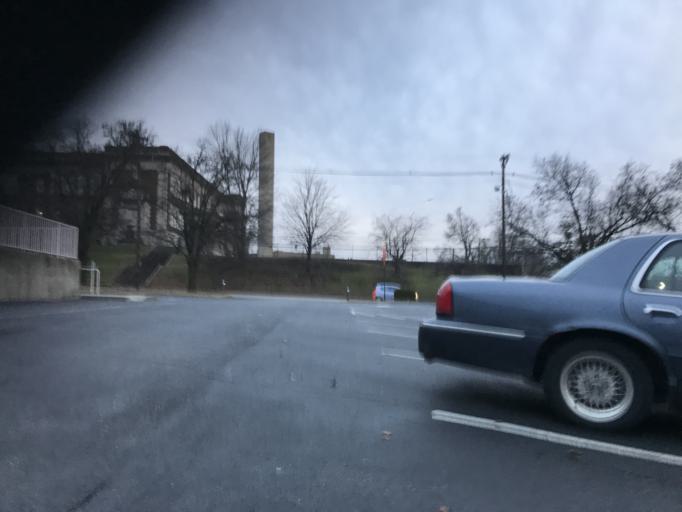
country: US
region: Kentucky
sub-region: Jefferson County
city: Louisville
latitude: 38.2447
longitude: -85.7330
